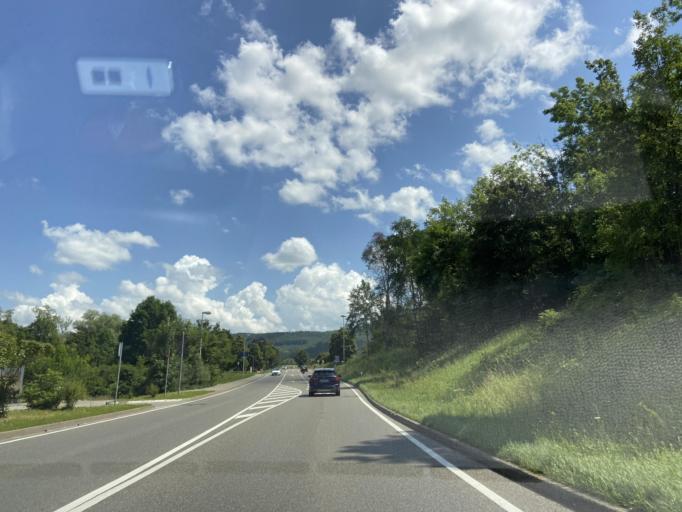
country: DE
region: Baden-Wuerttemberg
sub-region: Tuebingen Region
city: Messstetten
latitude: 48.2194
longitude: 8.9226
